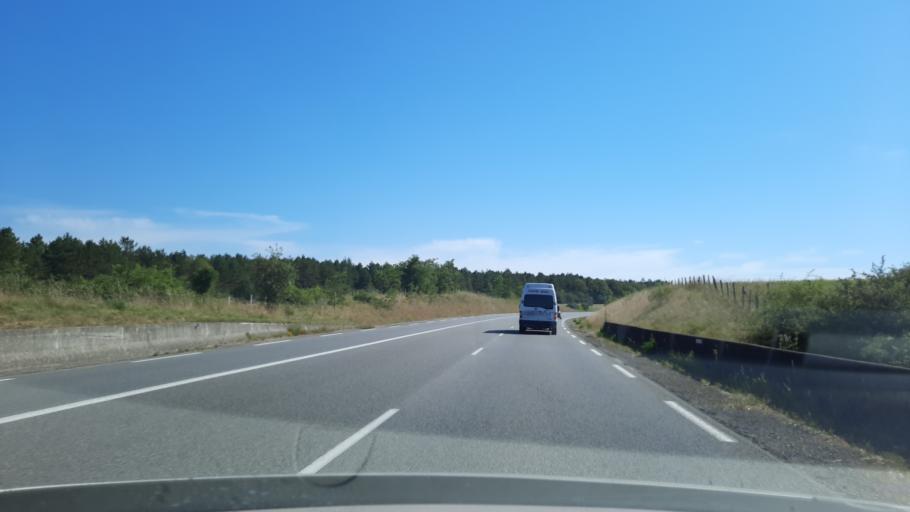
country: FR
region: Midi-Pyrenees
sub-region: Departement de l'Aveyron
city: Villefranche-de-Rouergue
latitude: 44.3407
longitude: 1.9405
